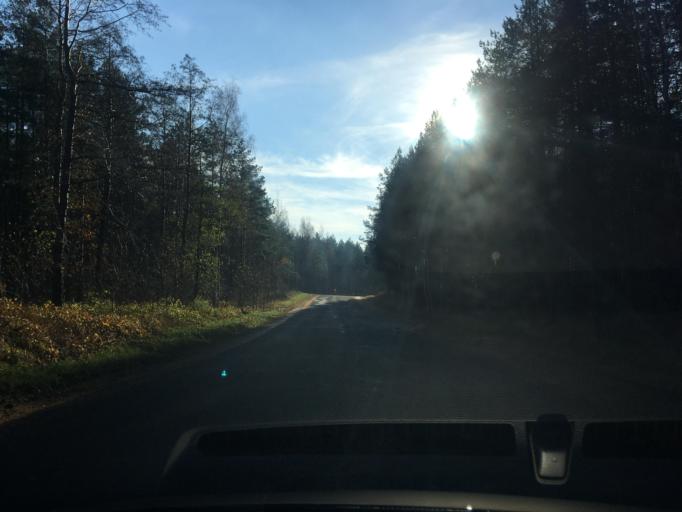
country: EE
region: Harju
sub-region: Maardu linn
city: Maardu
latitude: 59.4698
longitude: 25.0265
